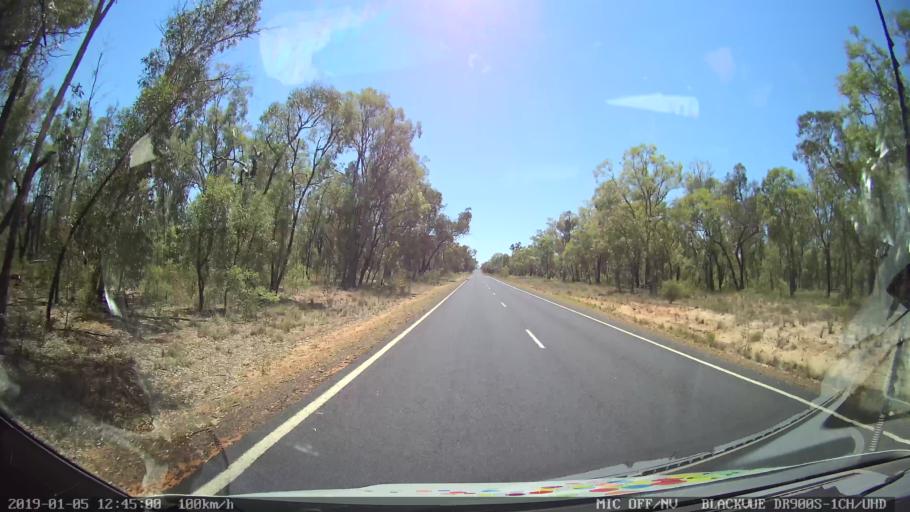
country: AU
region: New South Wales
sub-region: Warrumbungle Shire
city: Coonabarabran
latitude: -31.1321
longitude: 149.5445
